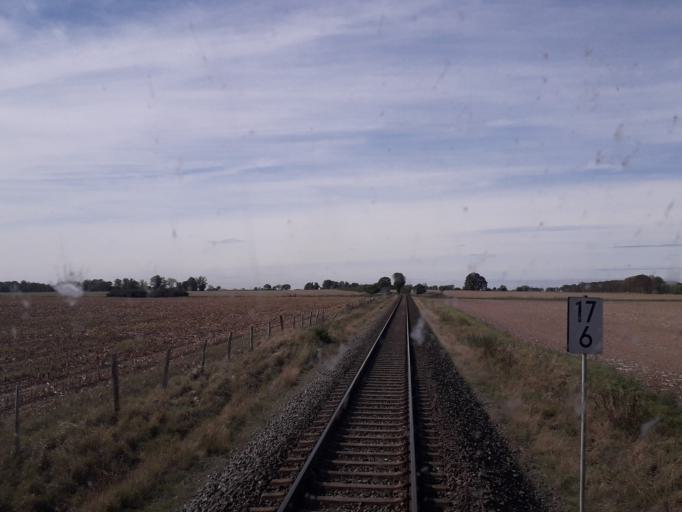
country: DE
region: Brandenburg
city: Ruthnick
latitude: 52.8612
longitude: 12.8897
